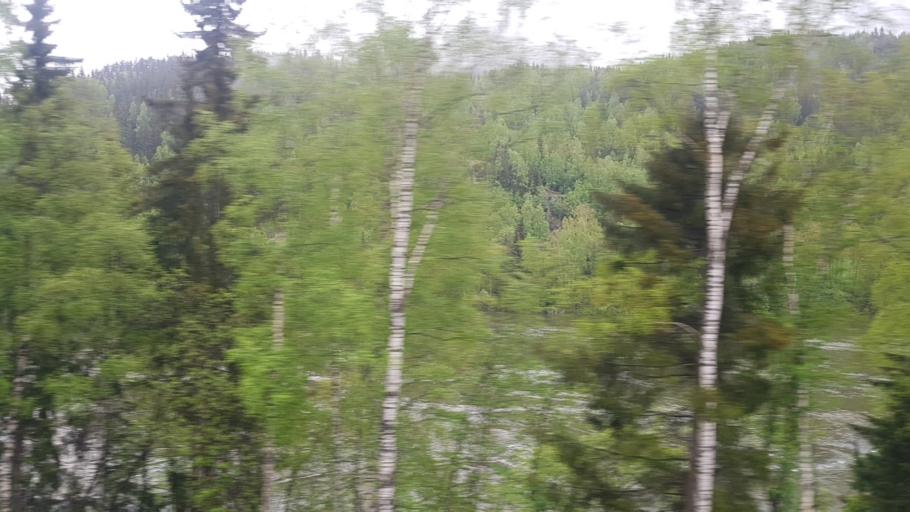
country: NO
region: Oppland
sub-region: Oyer
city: Tretten
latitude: 61.3256
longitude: 10.2932
